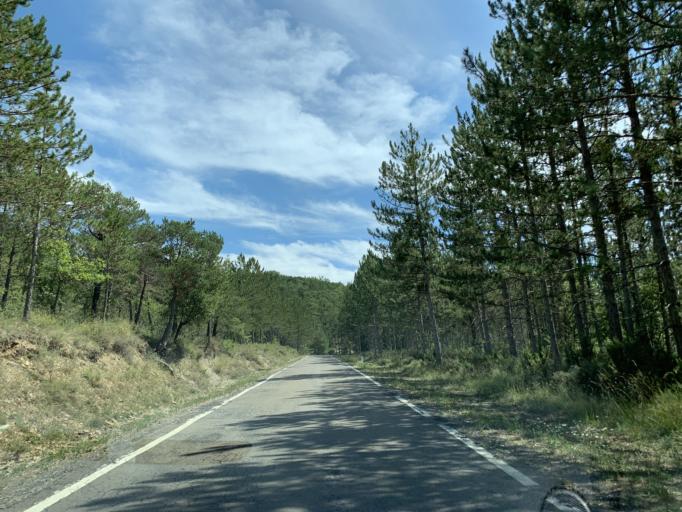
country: ES
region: Aragon
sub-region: Provincia de Huesca
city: Santa Cruz de la Seros
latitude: 42.6054
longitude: -0.6576
